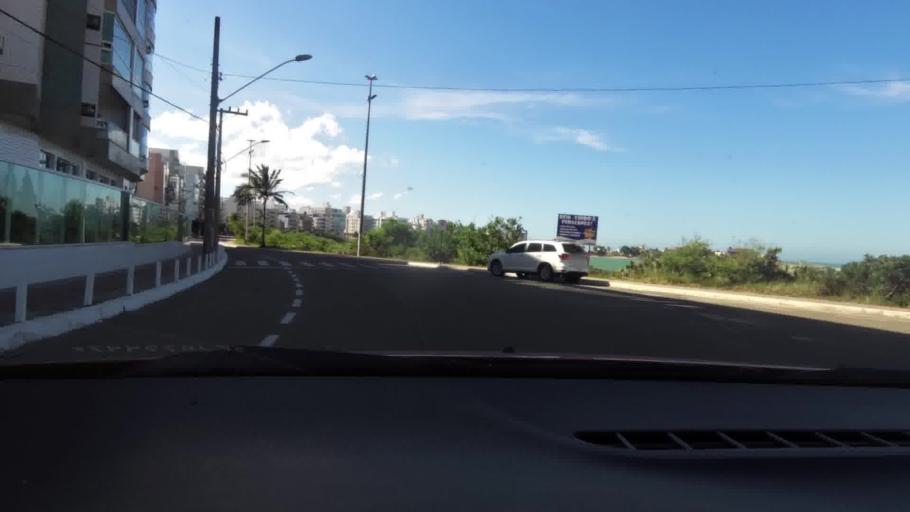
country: BR
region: Espirito Santo
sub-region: Guarapari
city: Guarapari
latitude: -20.7323
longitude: -40.5292
